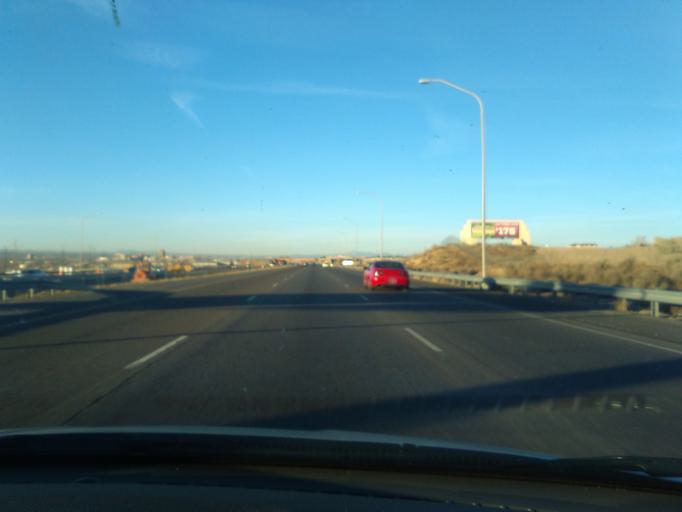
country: US
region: New Mexico
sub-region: Bernalillo County
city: South Valley
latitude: 35.0373
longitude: -106.6379
